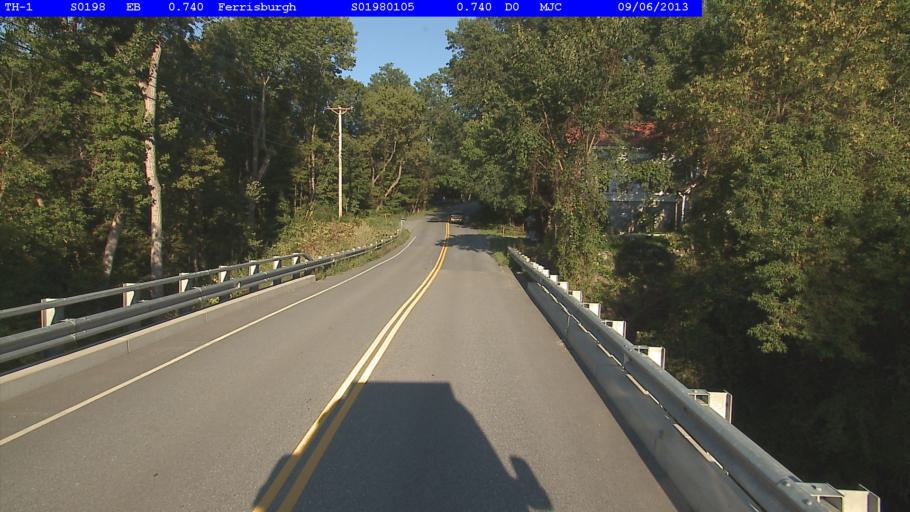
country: US
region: Vermont
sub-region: Addison County
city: Vergennes
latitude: 44.2594
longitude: -73.2134
